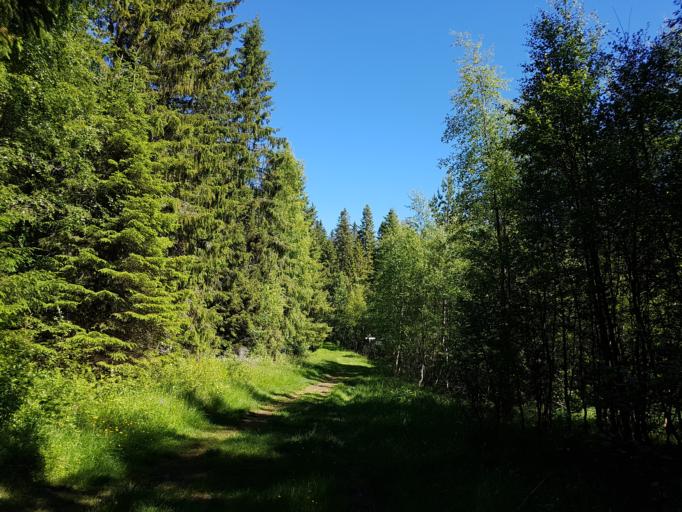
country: NO
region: Sor-Trondelag
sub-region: Melhus
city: Melhus
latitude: 63.4308
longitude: 10.2010
